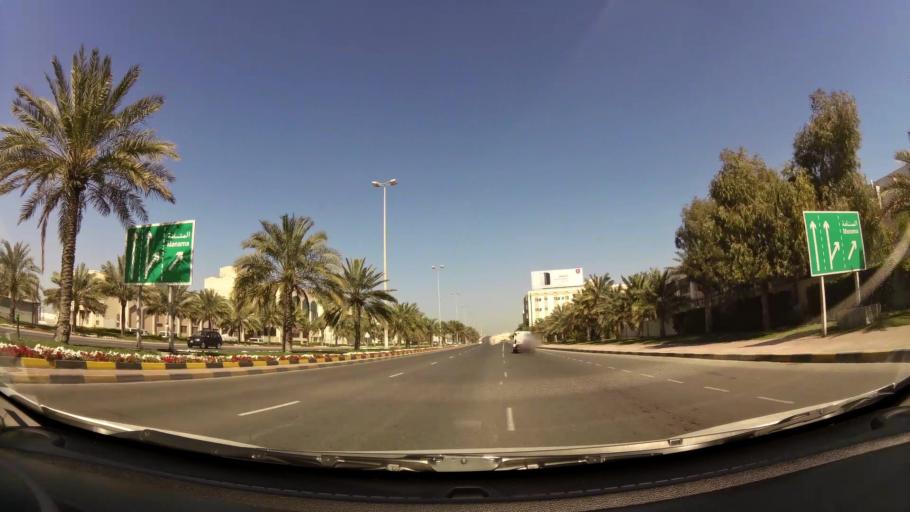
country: BH
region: Muharraq
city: Al Muharraq
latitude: 26.2457
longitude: 50.6092
